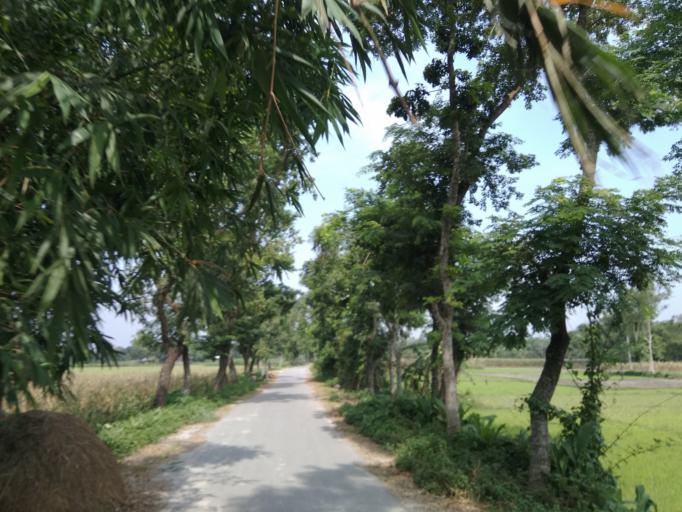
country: BD
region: Rangpur Division
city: Rangpur
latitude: 25.8363
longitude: 89.2001
